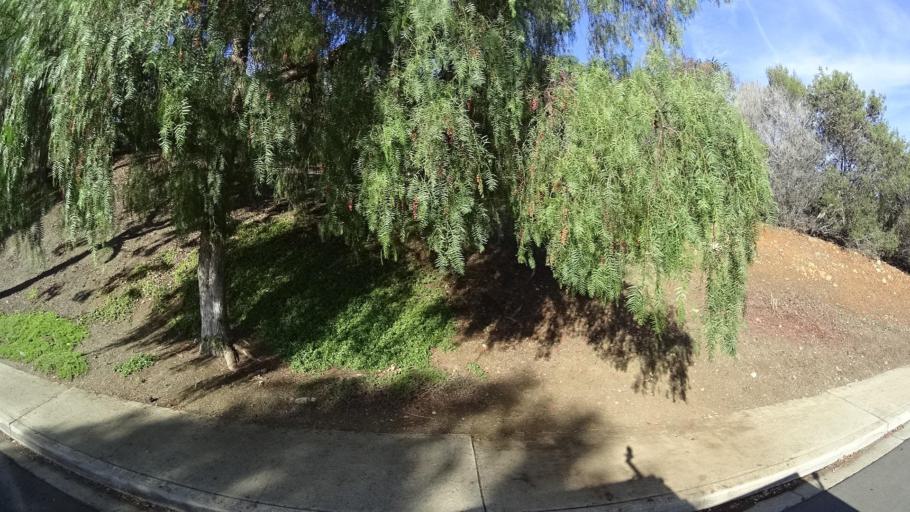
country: US
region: California
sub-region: San Diego County
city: Rancho San Diego
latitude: 32.7392
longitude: -116.9594
